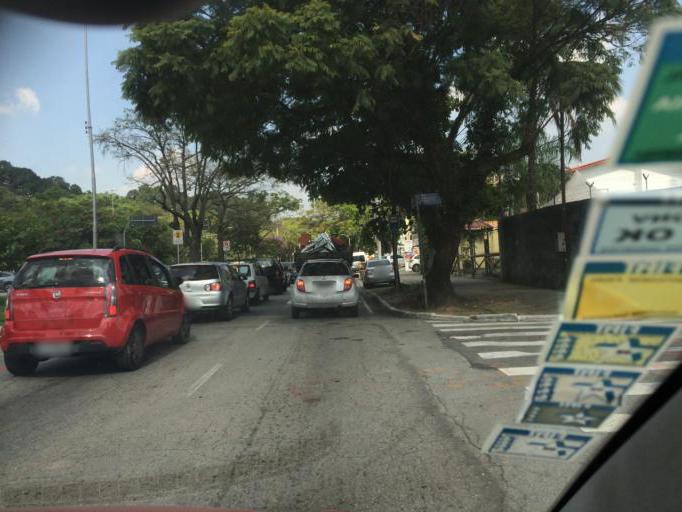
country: BR
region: Sao Paulo
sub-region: Guarulhos
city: Guarulhos
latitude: -23.4575
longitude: -46.5308
